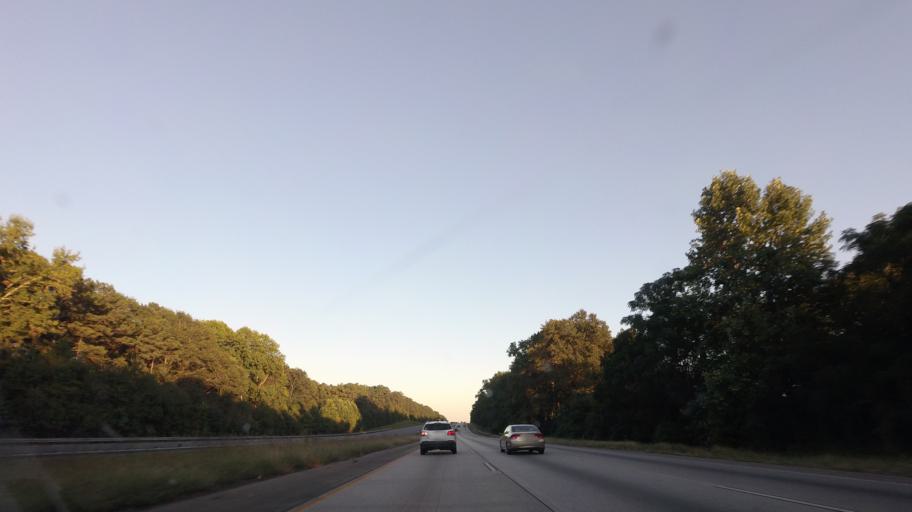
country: US
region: Georgia
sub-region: Monroe County
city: Forsyth
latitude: 33.0182
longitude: -83.8913
